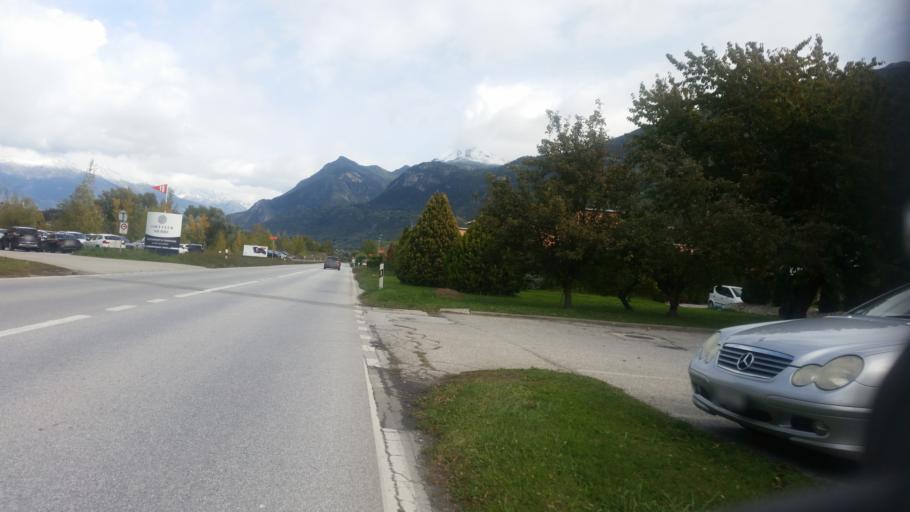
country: CH
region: Valais
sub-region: Sierre District
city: Grone
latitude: 46.2542
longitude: 7.4537
